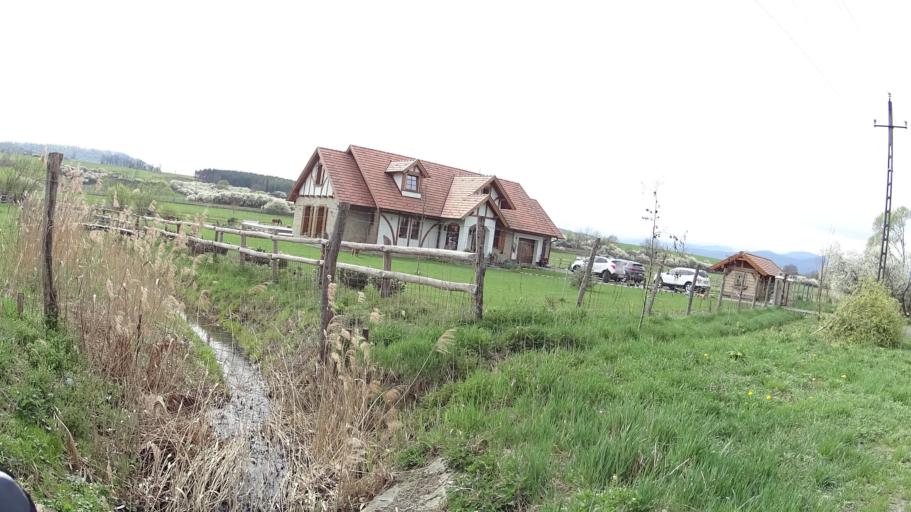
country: HU
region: Nograd
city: Diosjeno
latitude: 47.8932
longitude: 19.0631
